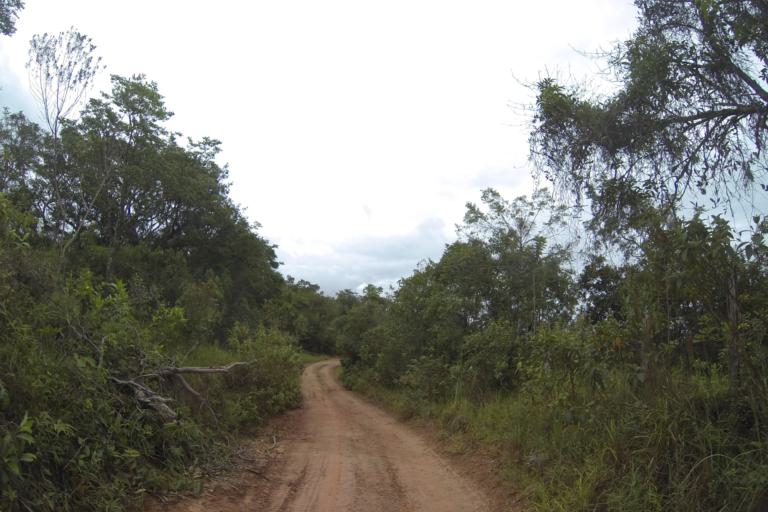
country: BR
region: Minas Gerais
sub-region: Ibia
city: Ibia
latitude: -19.7446
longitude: -46.5578
